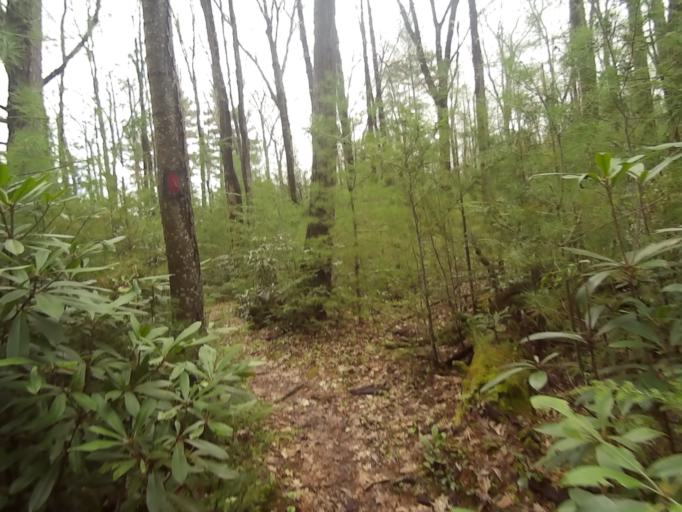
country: US
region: Pennsylvania
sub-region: Centre County
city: Boalsburg
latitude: 40.7316
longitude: -77.7530
